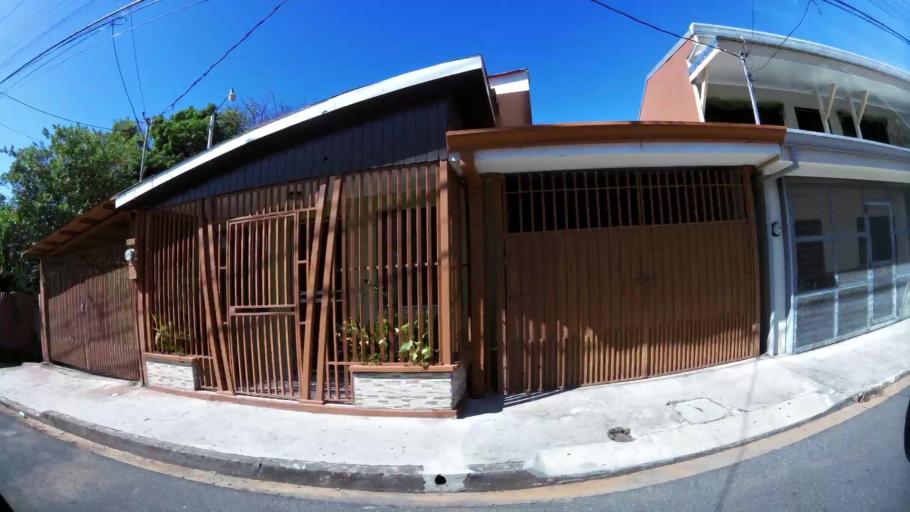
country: CR
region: Guanacaste
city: Liberia
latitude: 10.6338
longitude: -85.4364
